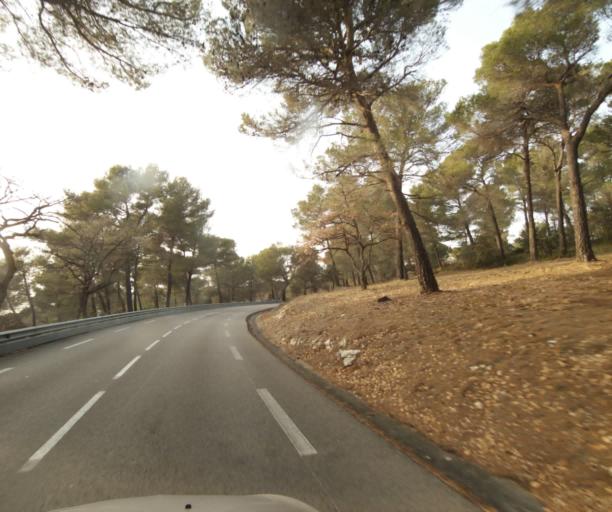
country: FR
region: Provence-Alpes-Cote d'Azur
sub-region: Departement des Bouches-du-Rhone
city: Rognes
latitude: 43.6192
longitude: 5.3550
